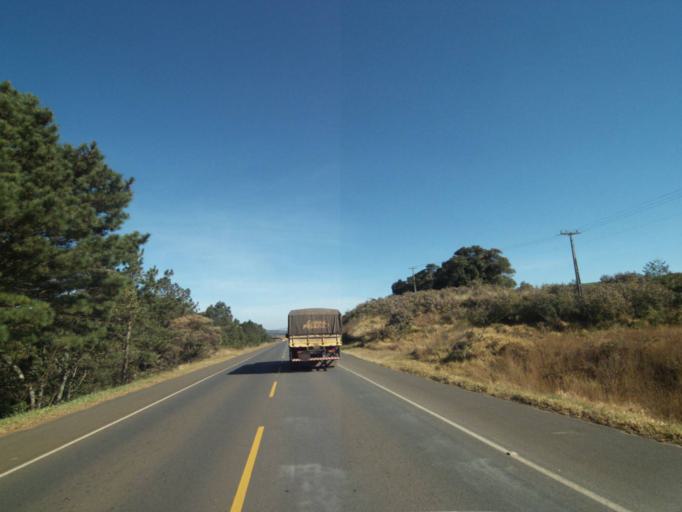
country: BR
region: Parana
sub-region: Tibagi
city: Tibagi
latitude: -24.3659
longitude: -50.3239
